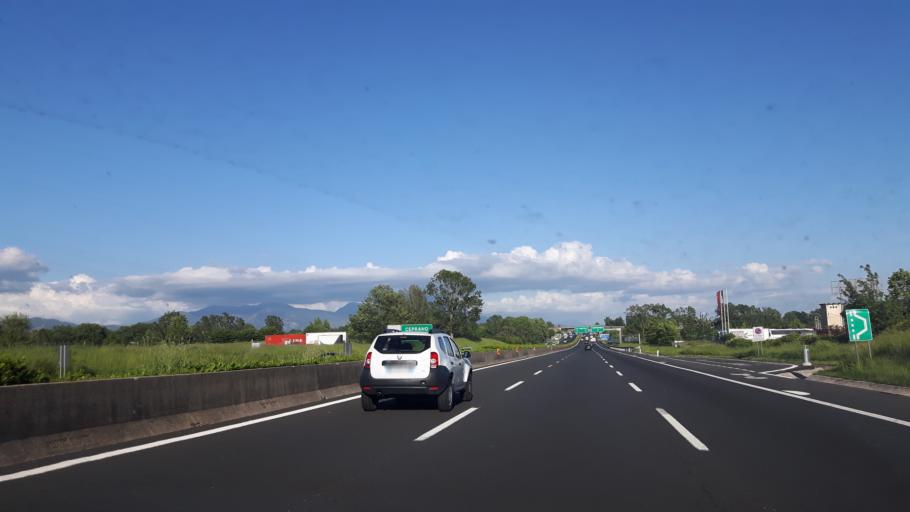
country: IT
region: Latium
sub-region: Provincia di Frosinone
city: Ceprano
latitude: 41.5464
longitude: 13.4778
